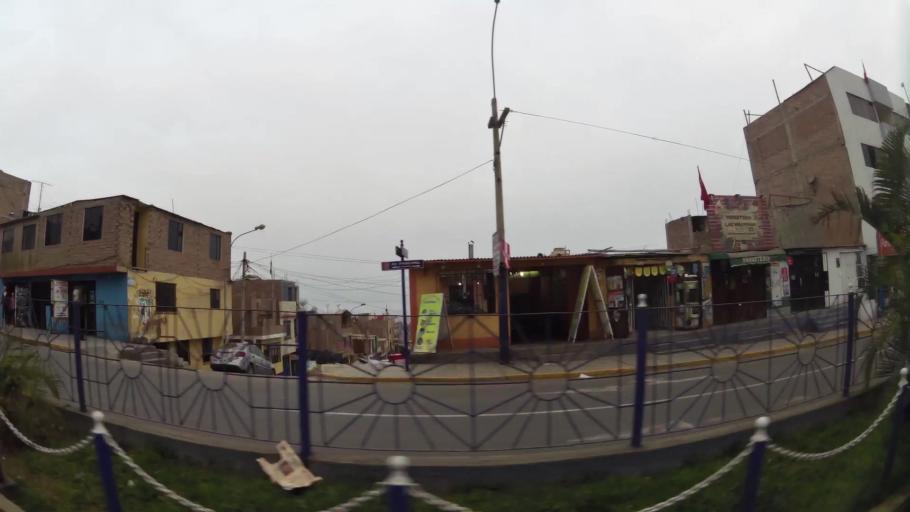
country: PE
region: Lima
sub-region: Lima
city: Surco
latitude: -12.1955
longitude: -77.0231
